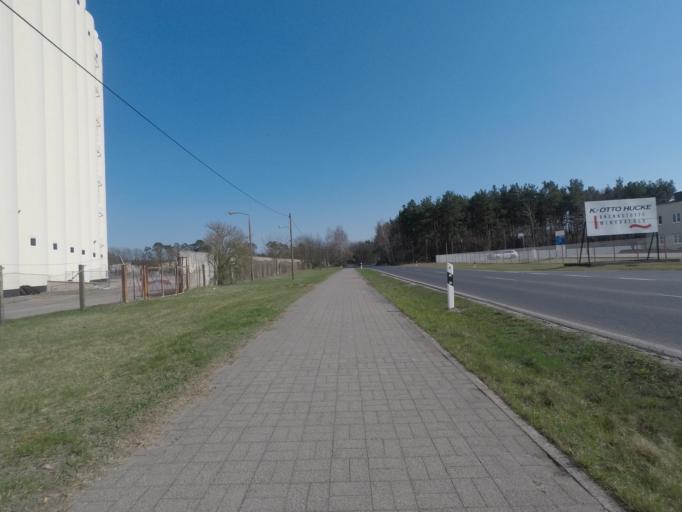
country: DE
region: Brandenburg
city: Eberswalde
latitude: 52.8480
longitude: 13.7871
